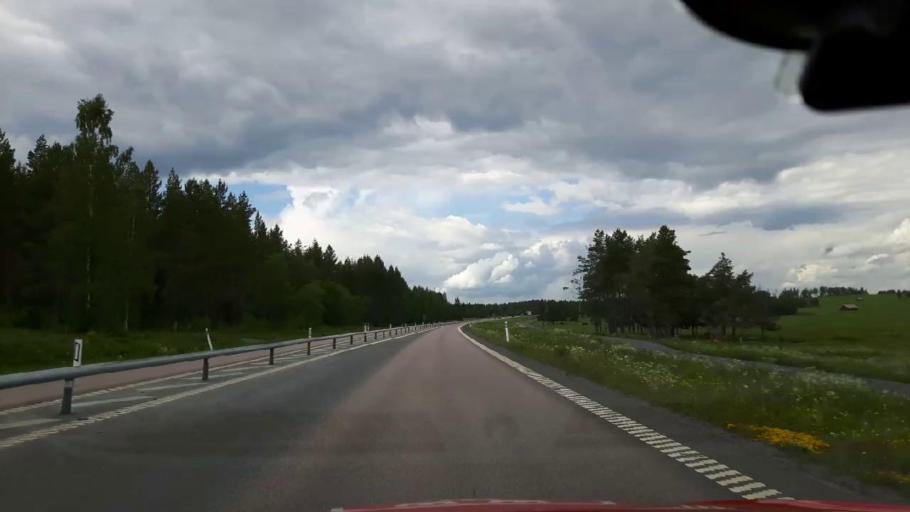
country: SE
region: Jaemtland
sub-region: OEstersunds Kommun
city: Ostersund
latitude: 63.2563
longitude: 14.5616
